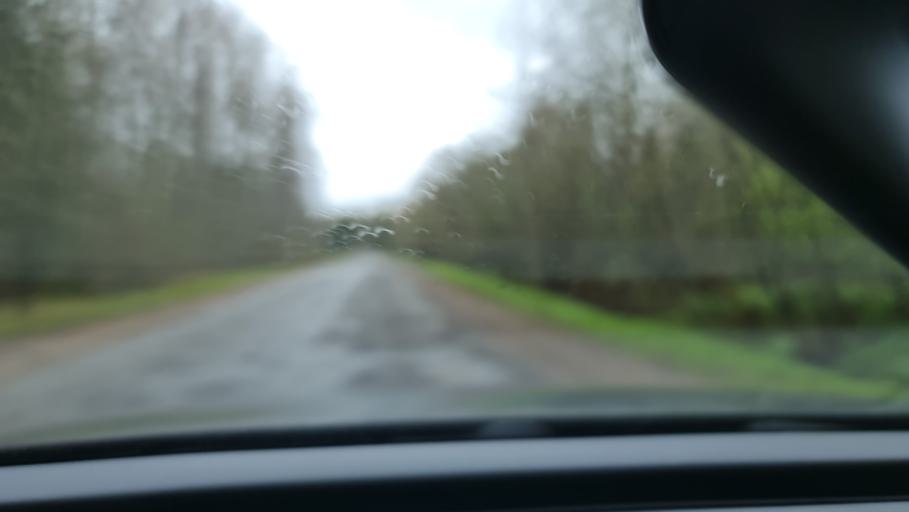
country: RU
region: Novgorod
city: Marevo
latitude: 57.2625
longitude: 32.0710
